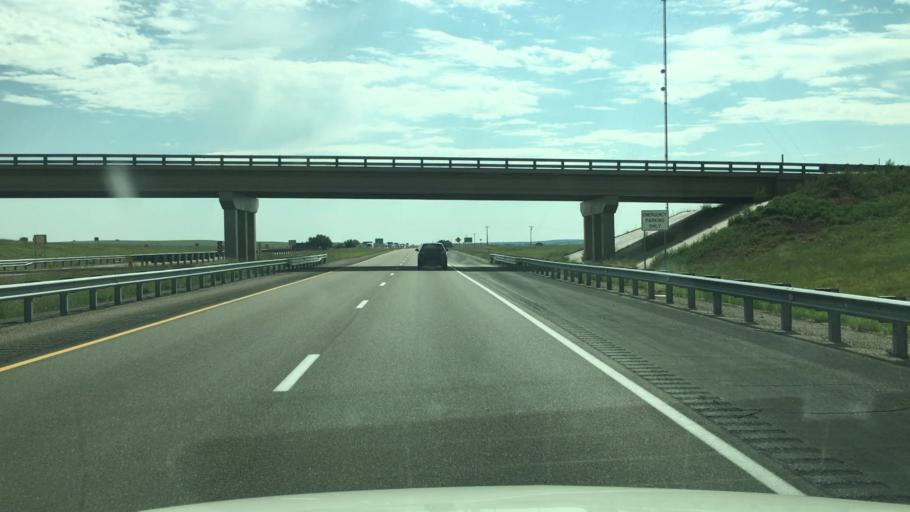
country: US
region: New Mexico
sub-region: San Miguel County
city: Las Vegas
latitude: 34.9912
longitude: -105.2942
